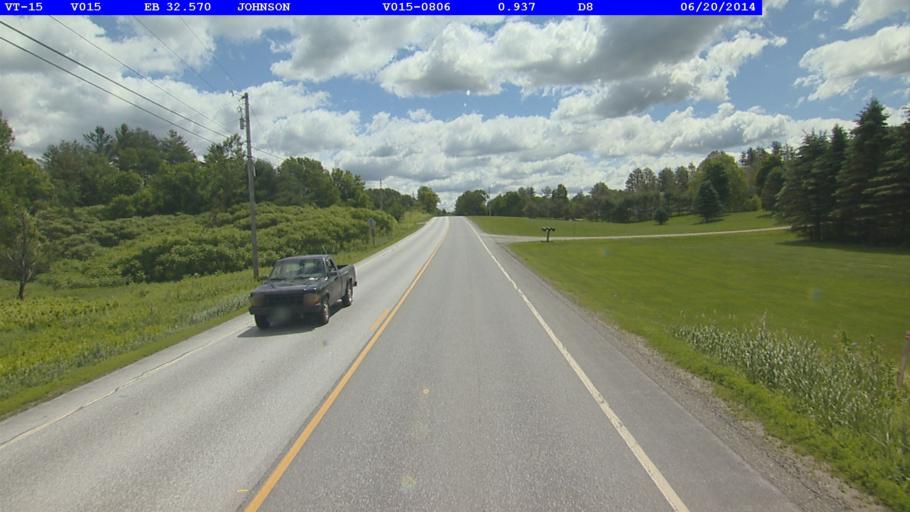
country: US
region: Vermont
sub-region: Lamoille County
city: Johnson
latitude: 44.6470
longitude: -72.7363
